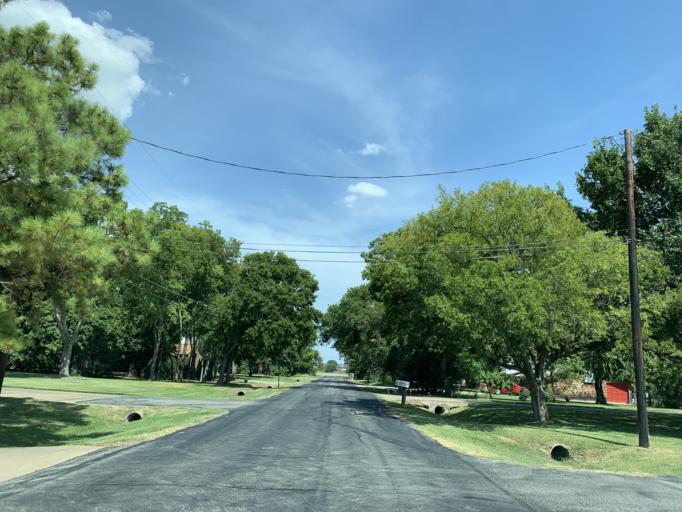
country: US
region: Texas
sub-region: Dallas County
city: Cedar Hill
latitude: 32.6489
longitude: -97.0166
